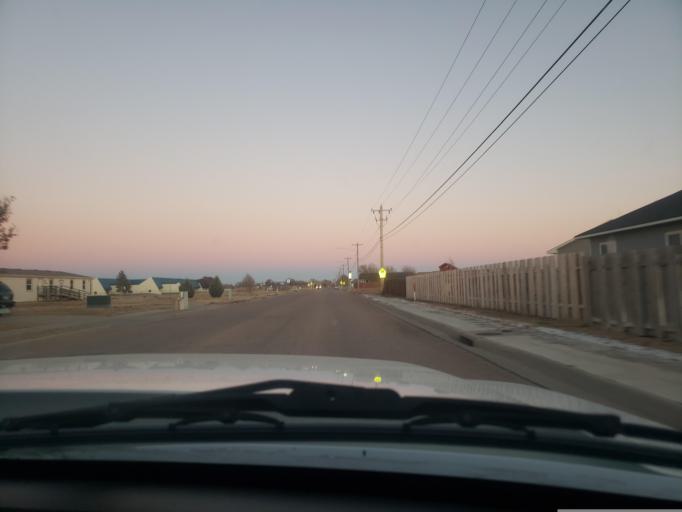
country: US
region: Kansas
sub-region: Finney County
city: Garden City
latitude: 37.9676
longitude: -100.8354
